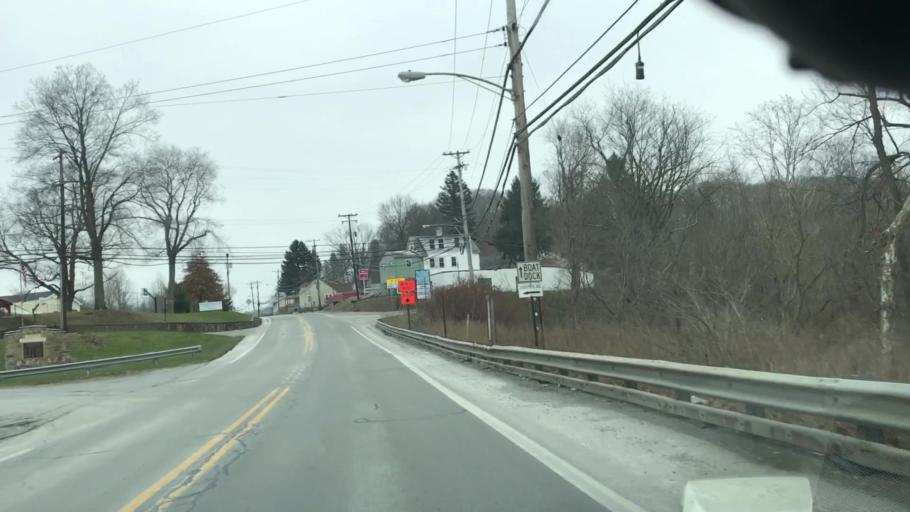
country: US
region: Pennsylvania
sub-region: Allegheny County
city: Coraopolis
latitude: 40.5046
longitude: -80.1436
